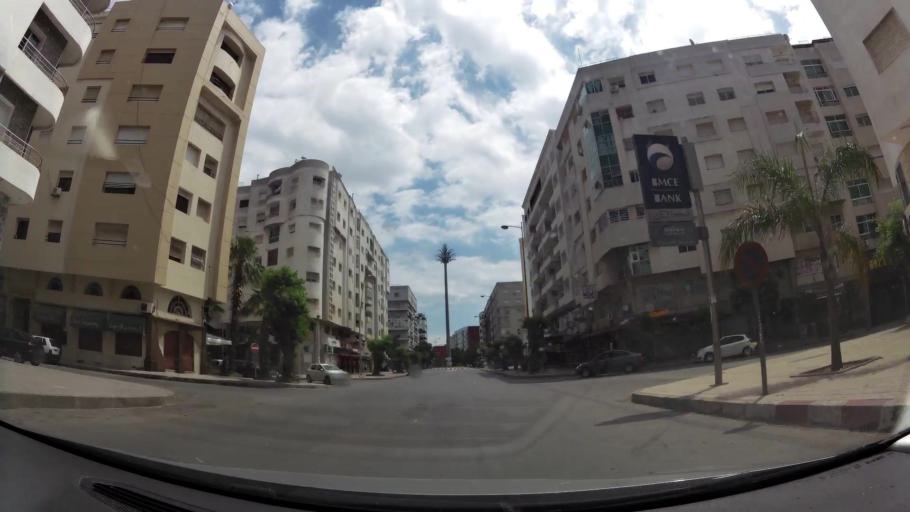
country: MA
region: Gharb-Chrarda-Beni Hssen
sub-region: Kenitra Province
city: Kenitra
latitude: 34.2602
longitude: -6.5908
